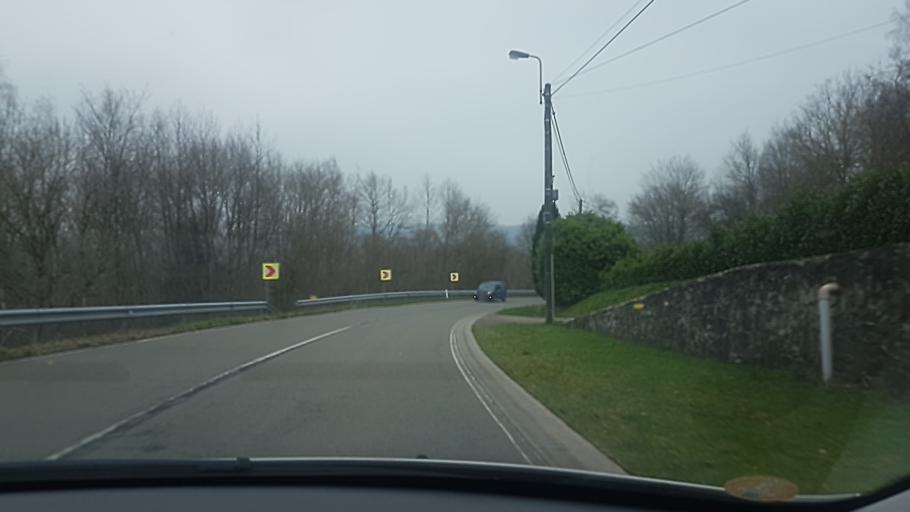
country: BE
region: Wallonia
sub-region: Province de Namur
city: Couvin
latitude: 50.0623
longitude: 4.6060
